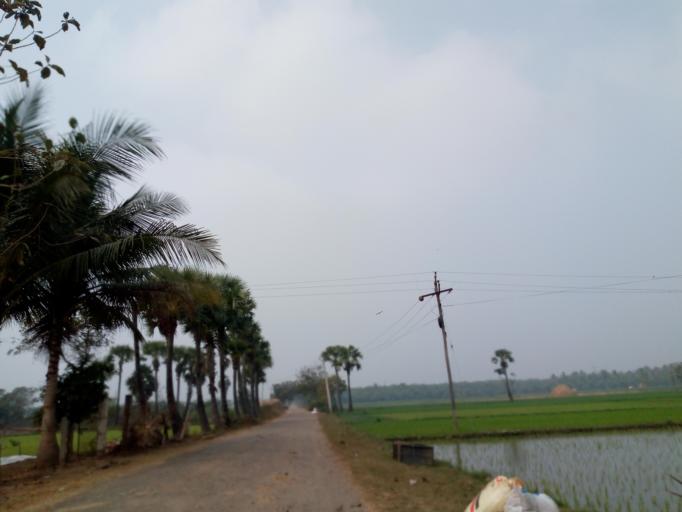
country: IN
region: Andhra Pradesh
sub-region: West Godavari
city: Tadepallegudem
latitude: 16.8647
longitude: 81.3101
